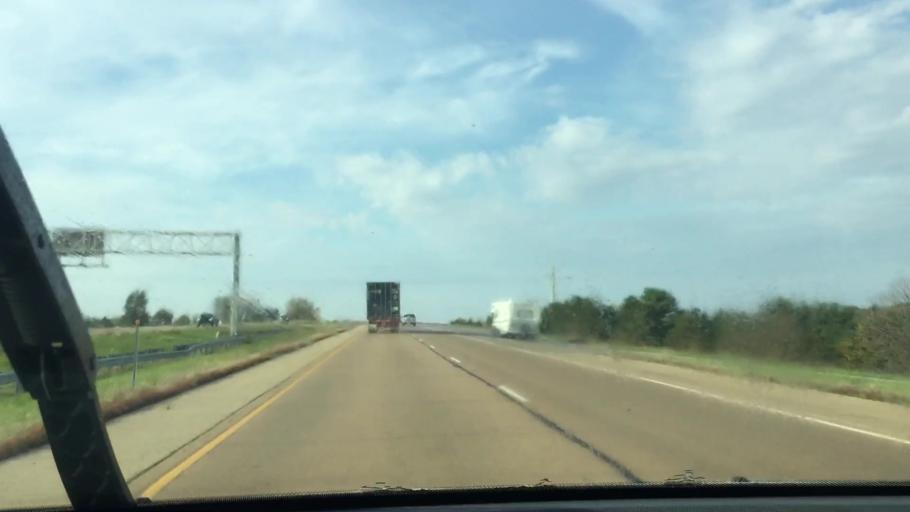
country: US
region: Illinois
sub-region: Whiteside County
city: Rock Falls
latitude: 41.7558
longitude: -89.6405
